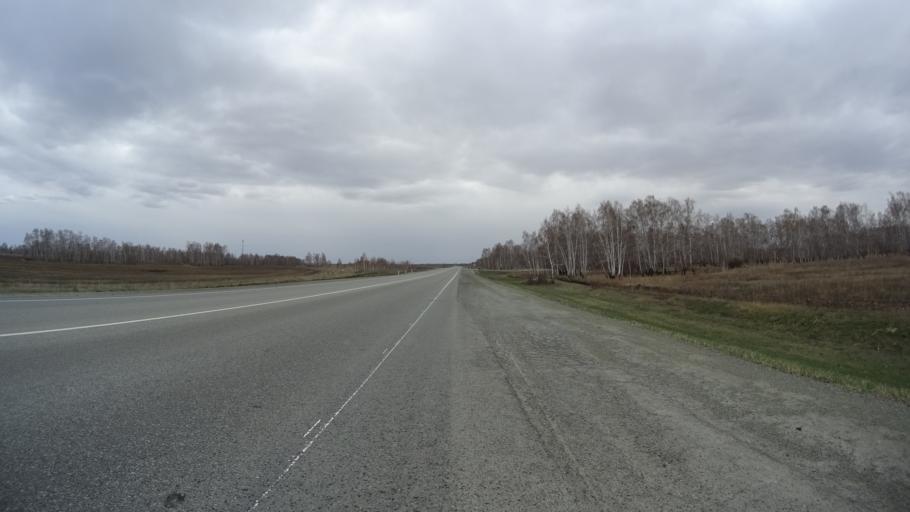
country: RU
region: Chelyabinsk
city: Krasnogorskiy
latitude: 54.6942
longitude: 61.2495
